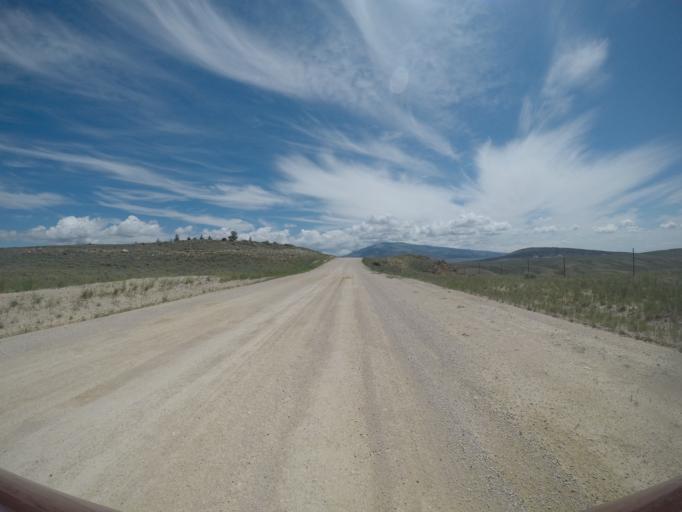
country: US
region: Wyoming
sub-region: Park County
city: Powell
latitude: 45.2065
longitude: -108.7744
